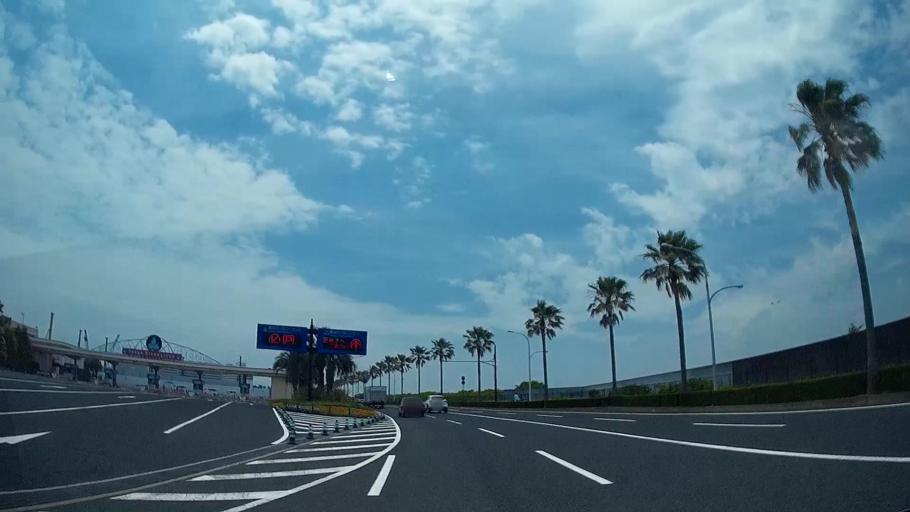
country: JP
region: Tokyo
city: Urayasu
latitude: 35.6379
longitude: 139.8760
